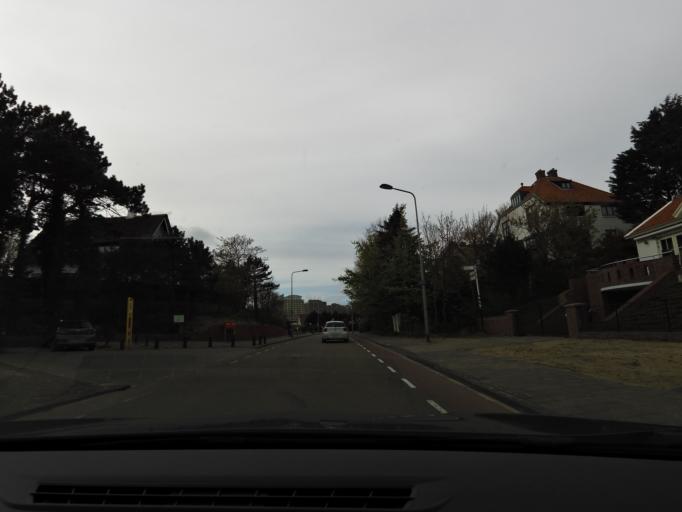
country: NL
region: South Holland
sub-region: Gemeente Noordwijk
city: Noordwijk-Binnen
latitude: 52.2384
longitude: 4.4338
